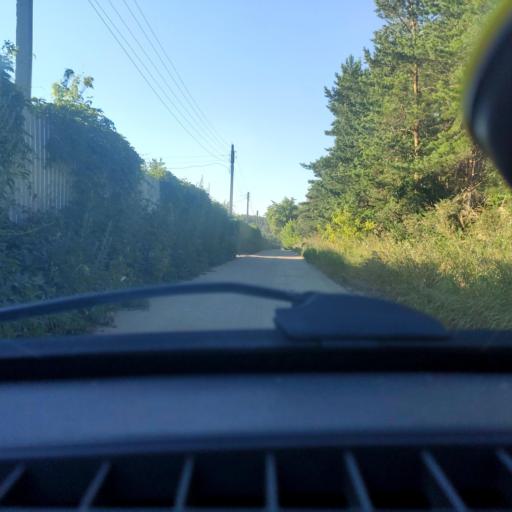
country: RU
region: Samara
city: Zhigulevsk
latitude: 53.4992
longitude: 49.5040
